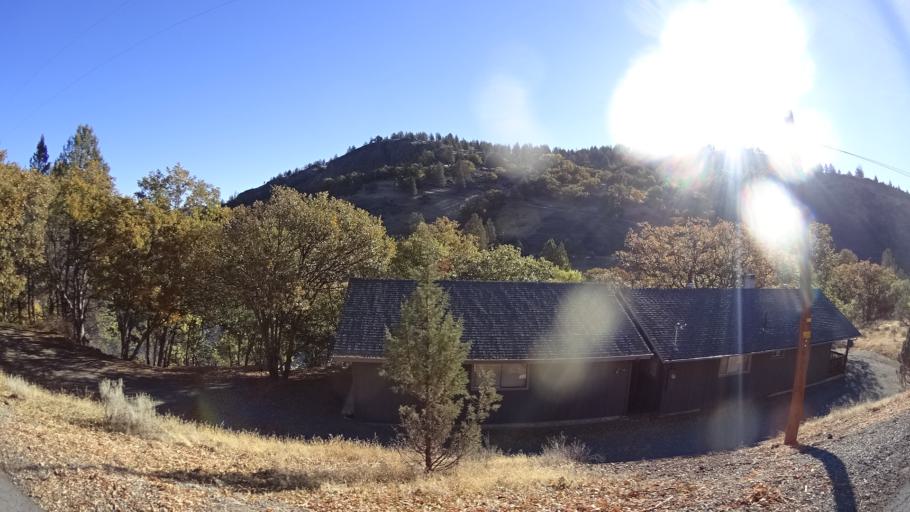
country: US
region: California
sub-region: Siskiyou County
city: Montague
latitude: 41.9233
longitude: -122.4493
